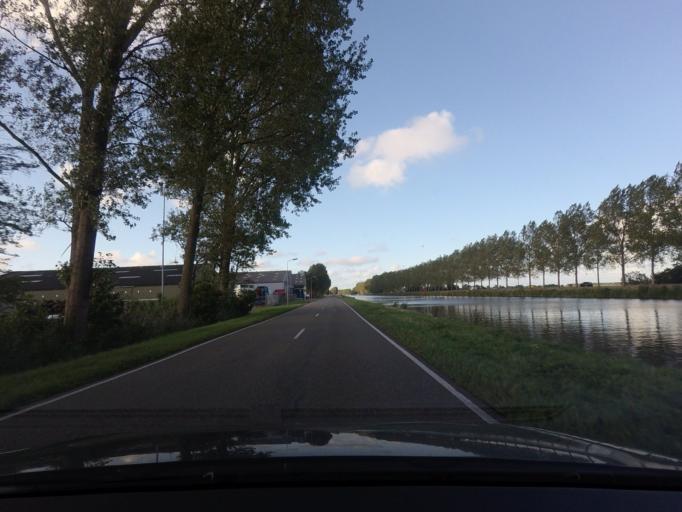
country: NL
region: North Holland
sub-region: Gemeente Alkmaar
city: Alkmaar
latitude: 52.5973
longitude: 4.7593
